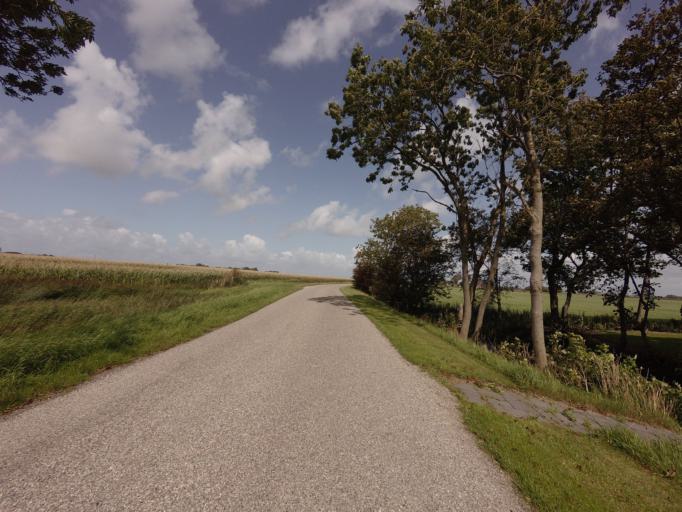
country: NL
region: Friesland
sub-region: Gemeente Harlingen
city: Harlingen
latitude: 53.1552
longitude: 5.4792
